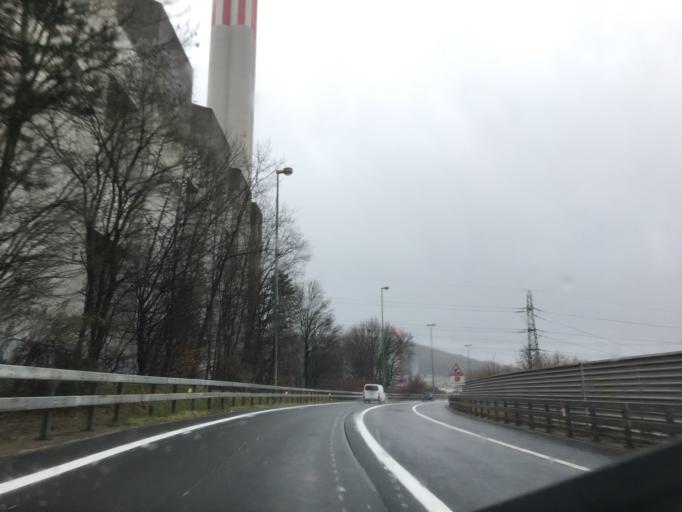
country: CH
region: Zurich
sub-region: Bezirk Zuerich
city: Zuerich (Kreis 12) / Auzelg
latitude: 47.4128
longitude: 8.5739
